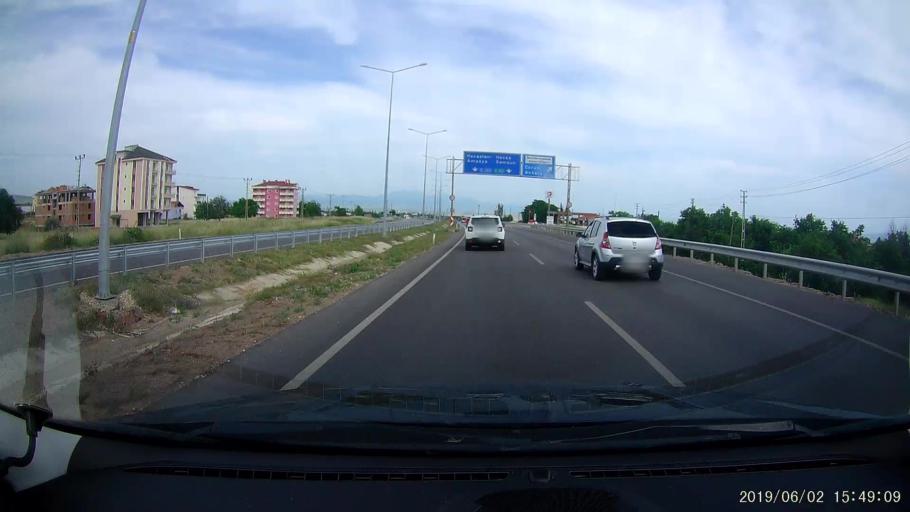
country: TR
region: Amasya
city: Merzifon
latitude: 40.8583
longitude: 35.4576
